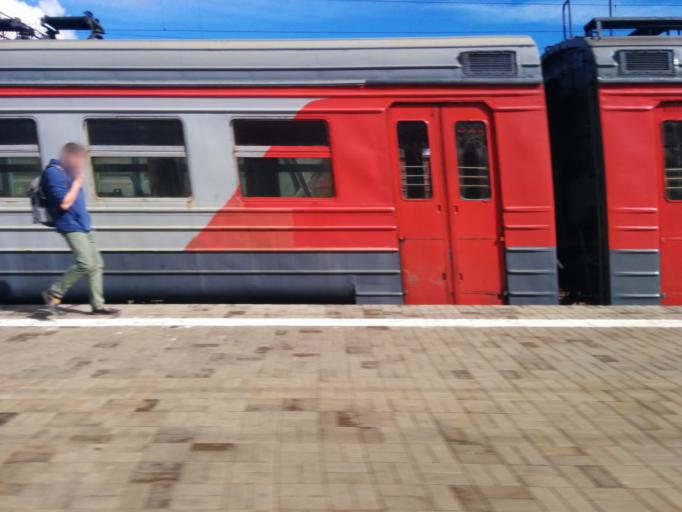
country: RU
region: Moskovskaya
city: Vostochnoe Degunino
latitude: 55.8837
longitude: 37.5677
